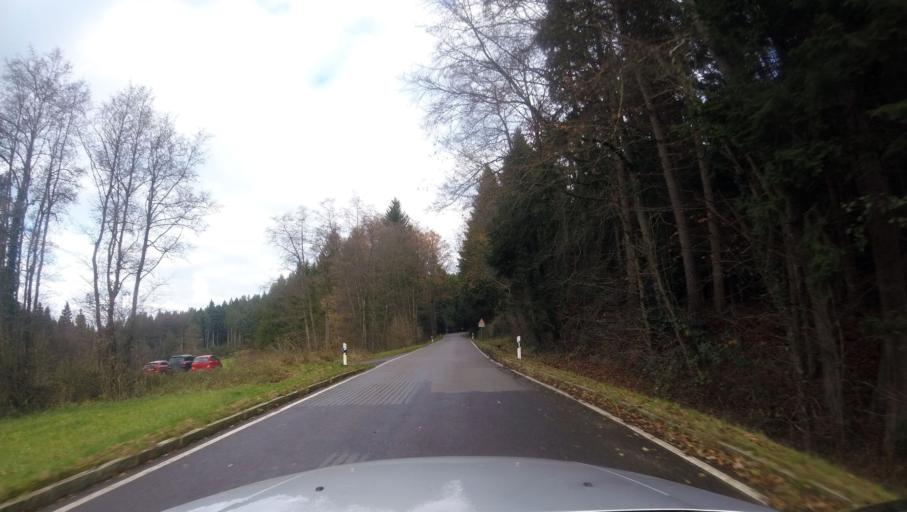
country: DE
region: Baden-Wuerttemberg
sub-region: Regierungsbezirk Stuttgart
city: Spraitbach
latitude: 48.8556
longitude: 9.7676
